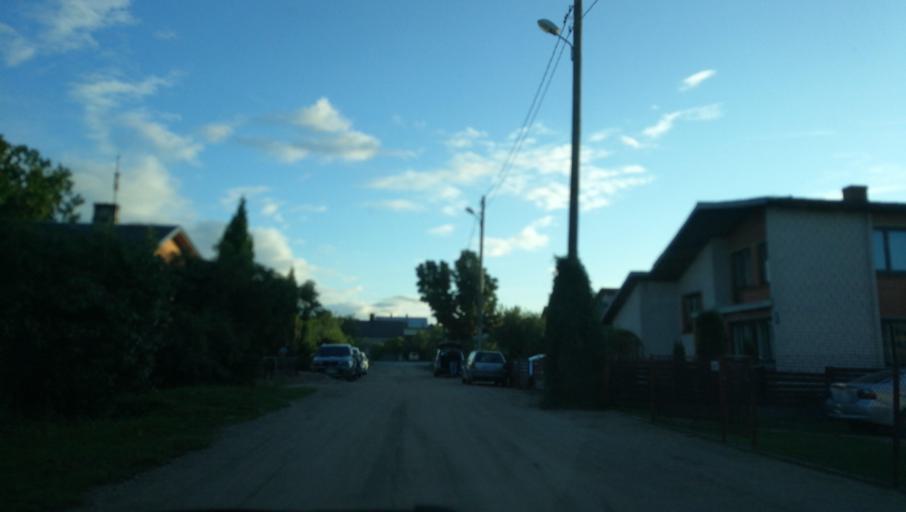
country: LV
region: Valmieras Rajons
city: Valmiera
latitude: 57.5333
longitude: 25.3918
